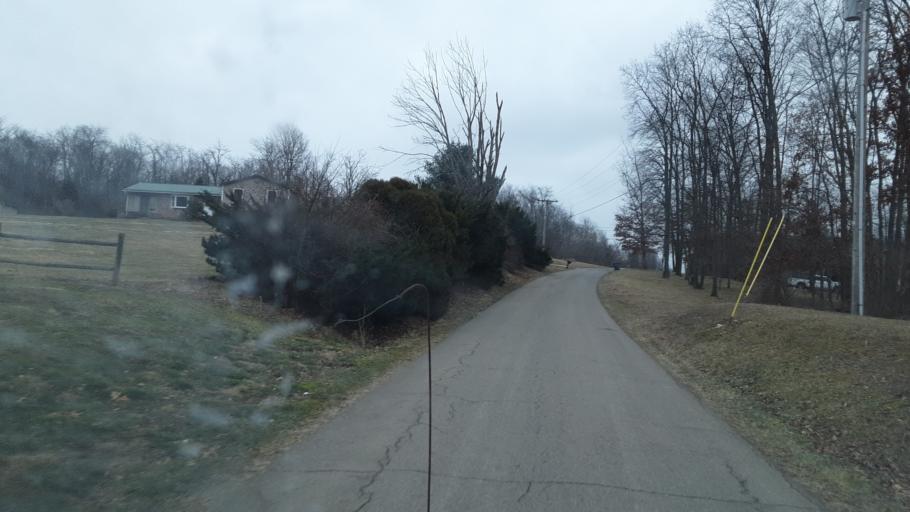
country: US
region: Ohio
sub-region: Perry County
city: Thornport
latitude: 39.9399
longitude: -82.3721
